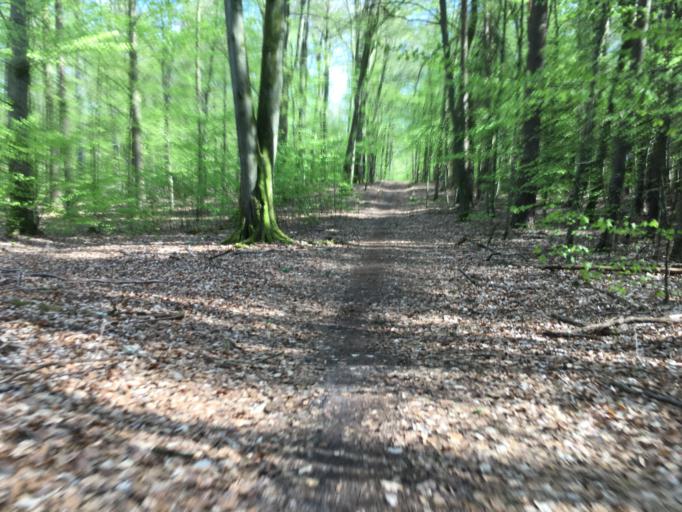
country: DE
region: Brandenburg
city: Bernau bei Berlin
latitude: 52.7346
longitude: 13.5631
